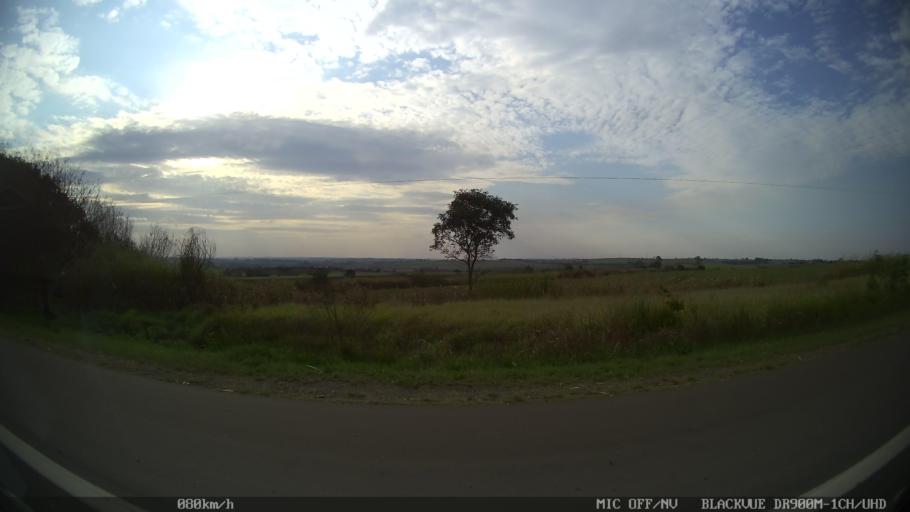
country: BR
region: Sao Paulo
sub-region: Cosmopolis
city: Cosmopolis
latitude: -22.6123
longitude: -47.2355
